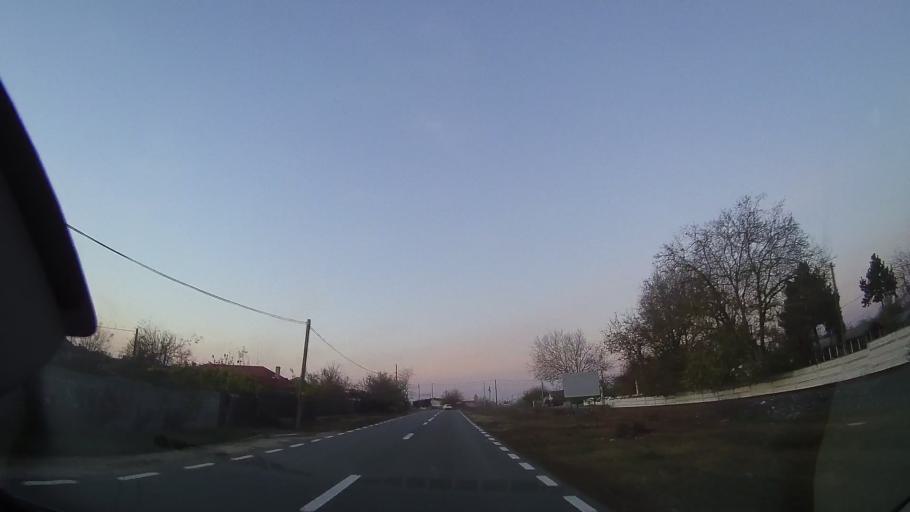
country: RO
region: Constanta
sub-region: Comuna Cobadin
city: Cobadin
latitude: 44.0540
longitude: 28.2466
